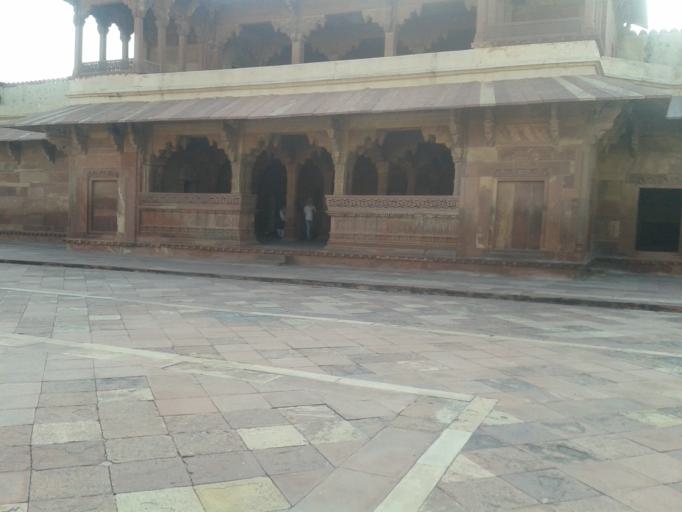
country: IN
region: Uttar Pradesh
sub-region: Agra
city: Fatehpur Sikri
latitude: 27.0966
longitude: 77.6648
